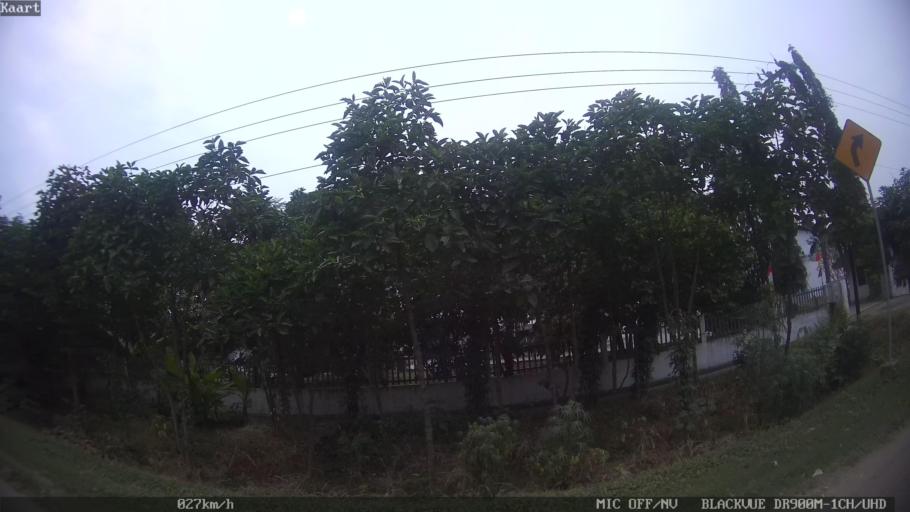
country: ID
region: Lampung
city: Panjang
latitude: -5.4347
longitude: 105.3244
